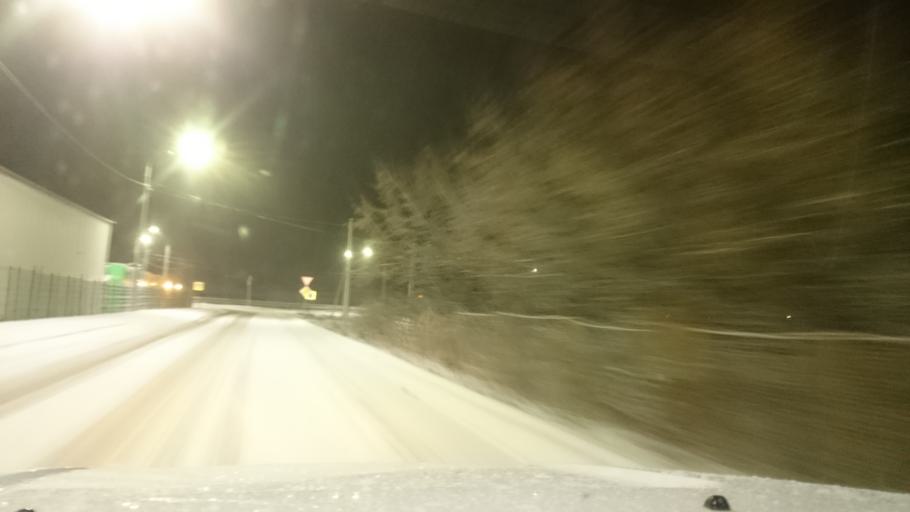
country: RU
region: Tula
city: Kosaya Gora
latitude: 54.1854
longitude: 37.5181
